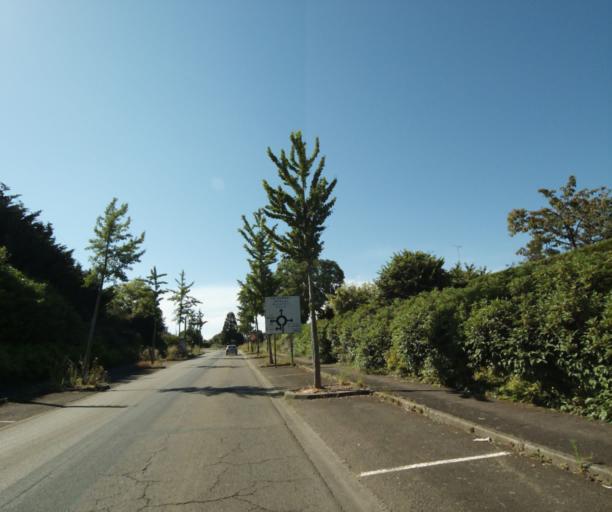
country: FR
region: Pays de la Loire
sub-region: Departement de la Mayenne
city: Laval
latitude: 48.0557
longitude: -0.7507
